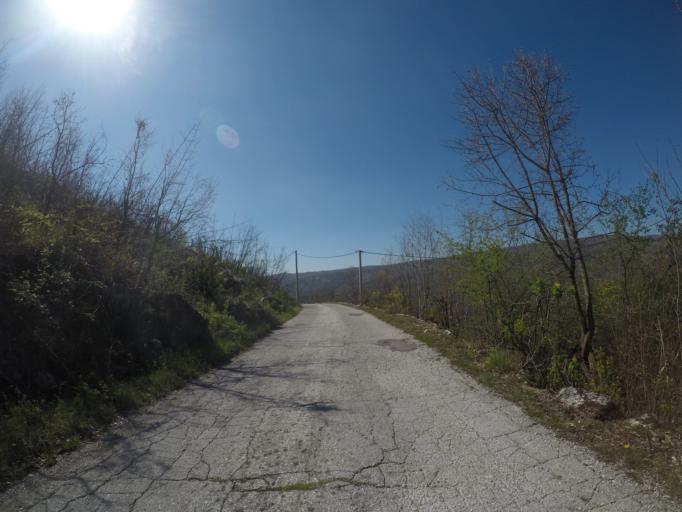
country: ME
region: Danilovgrad
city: Danilovgrad
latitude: 42.5305
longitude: 19.0269
